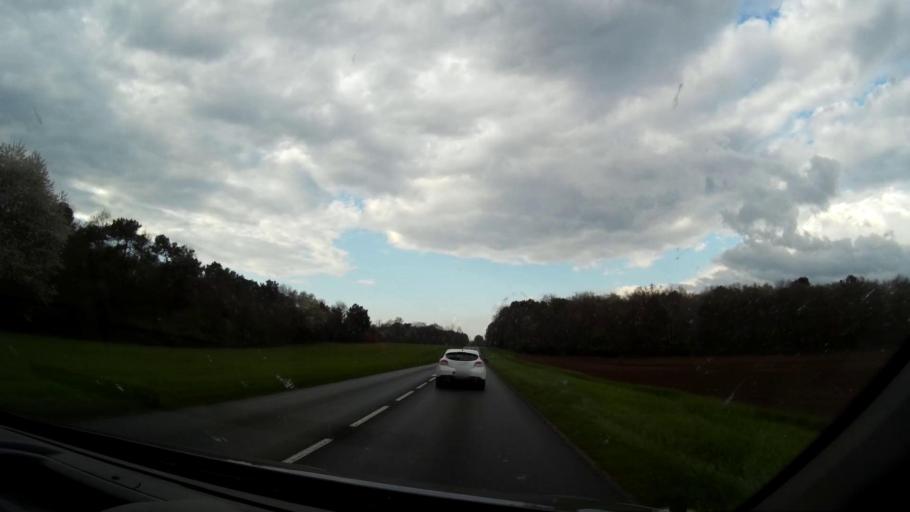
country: FR
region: Centre
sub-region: Departement du Loir-et-Cher
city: Cormeray
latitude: 47.4587
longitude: 1.4253
